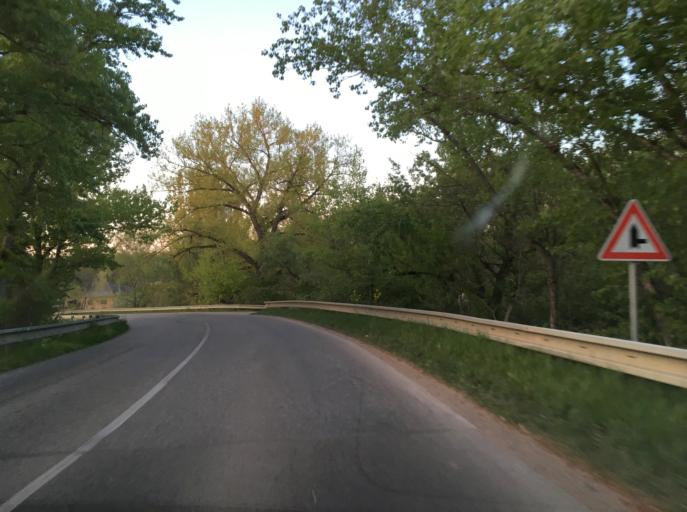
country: SK
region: Nitriansky
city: Kolarovo
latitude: 47.9154
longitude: 18.0116
